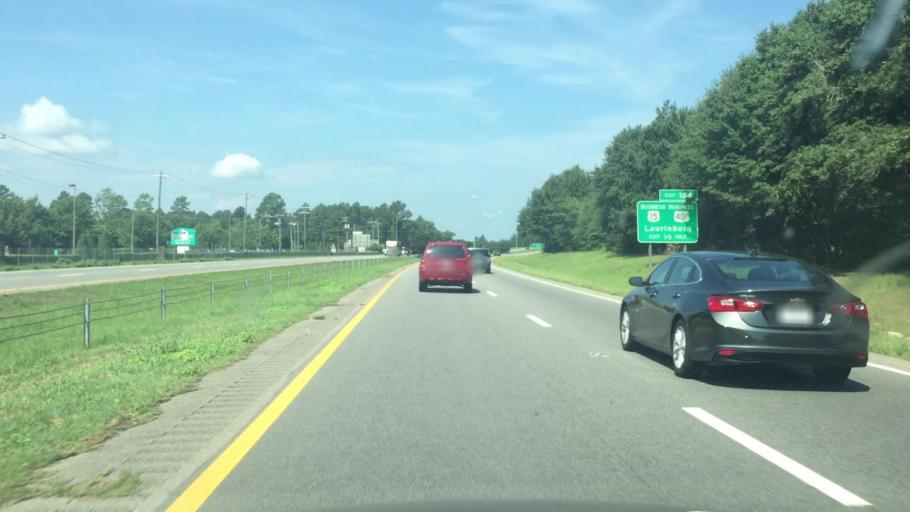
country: US
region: North Carolina
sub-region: Scotland County
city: Laurinburg
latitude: 34.7546
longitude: -79.4674
